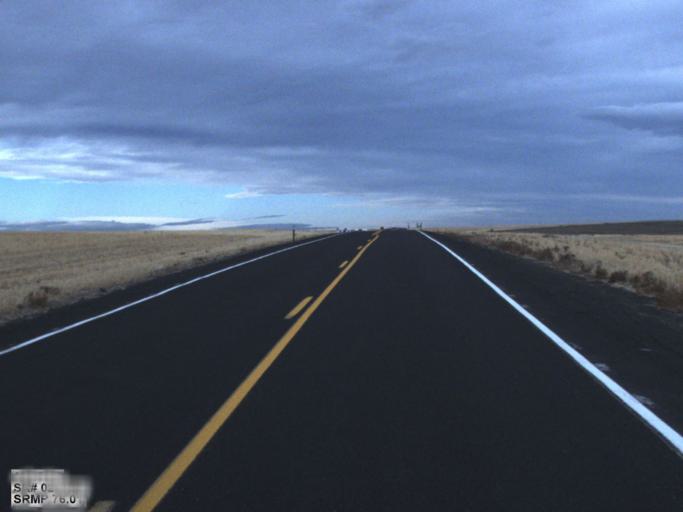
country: US
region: Washington
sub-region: Okanogan County
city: Coulee Dam
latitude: 47.5818
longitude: -118.7860
